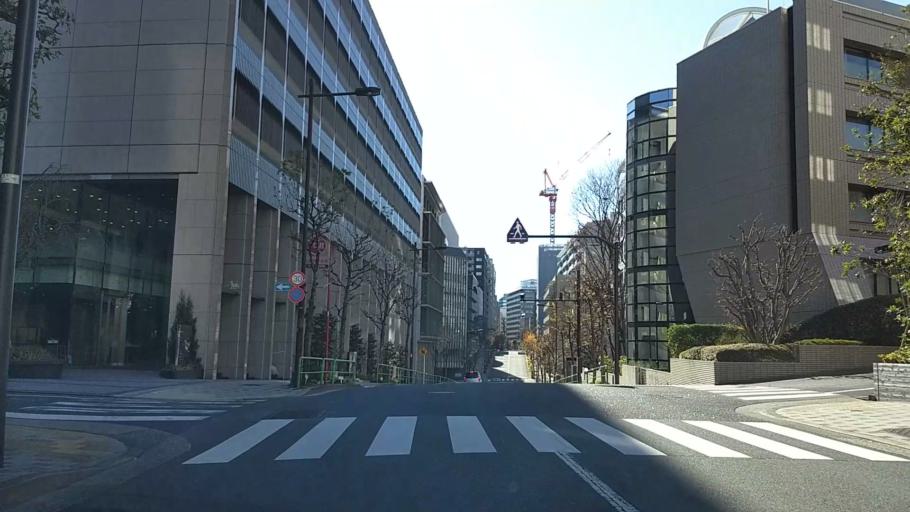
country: JP
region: Tokyo
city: Tokyo
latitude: 35.6917
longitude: 139.7436
